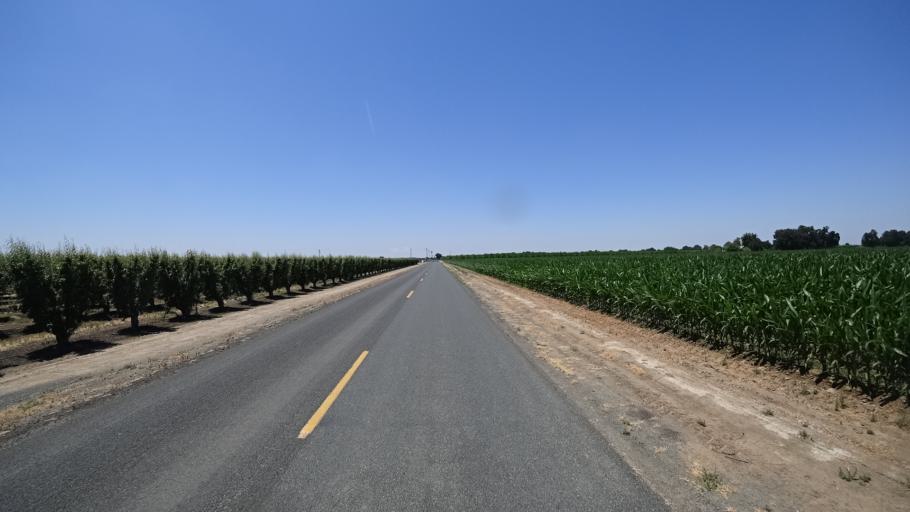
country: US
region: California
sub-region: Fresno County
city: Kingsburg
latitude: 36.4304
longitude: -119.5706
